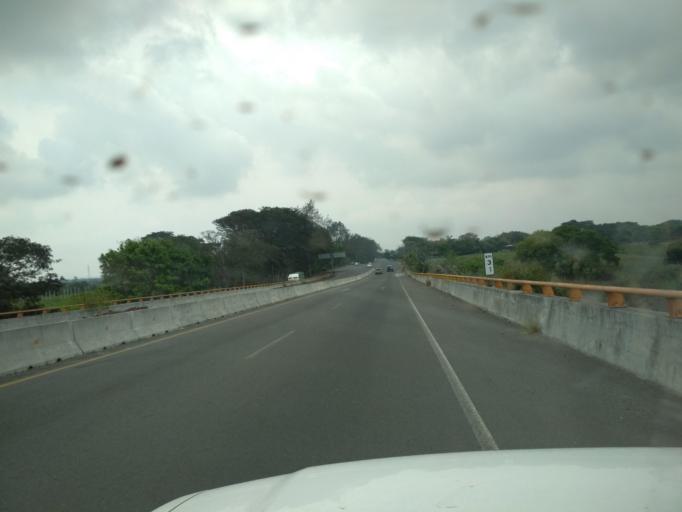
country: MX
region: Veracruz
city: Paso del Toro
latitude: 19.0211
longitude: -96.1324
